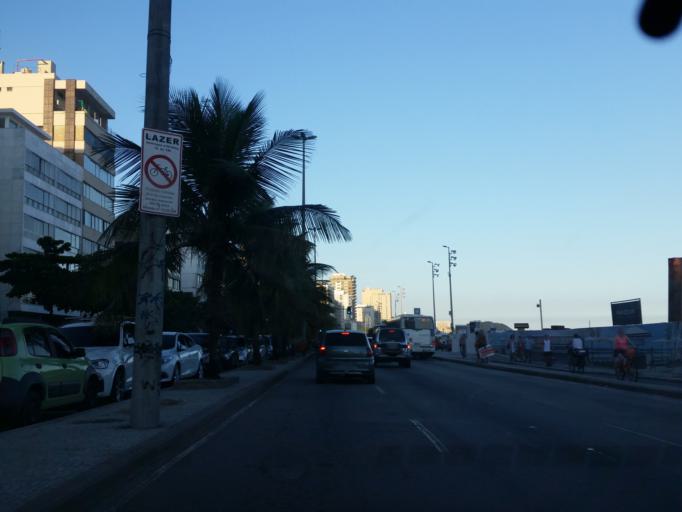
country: BR
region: Rio de Janeiro
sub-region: Rio De Janeiro
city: Rio de Janeiro
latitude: -22.9866
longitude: -43.2186
